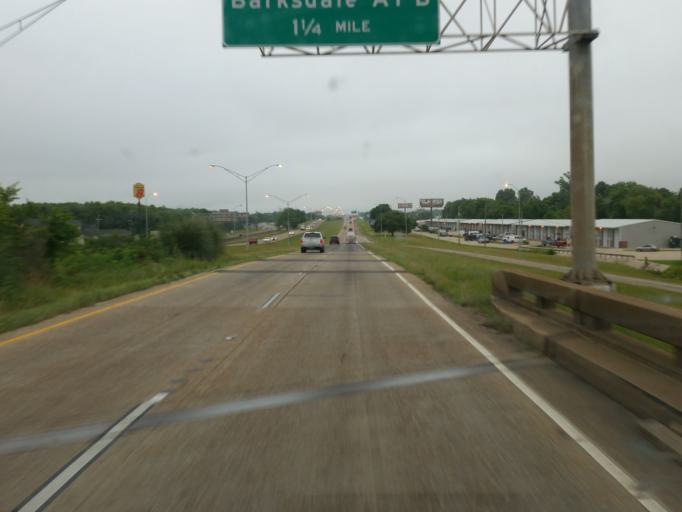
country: US
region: Louisiana
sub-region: Bossier Parish
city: Bossier City
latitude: 32.5254
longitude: -93.6989
